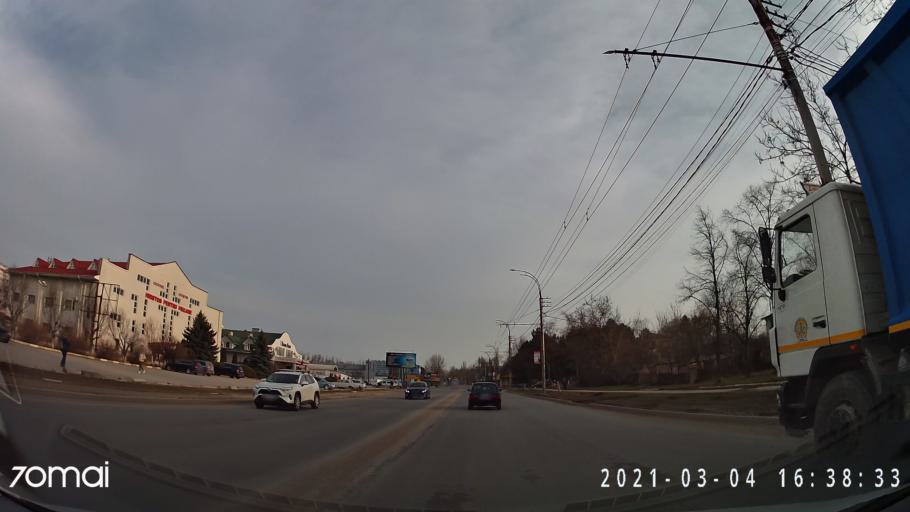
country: MD
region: Balti
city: Balti
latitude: 47.7803
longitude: 27.8915
